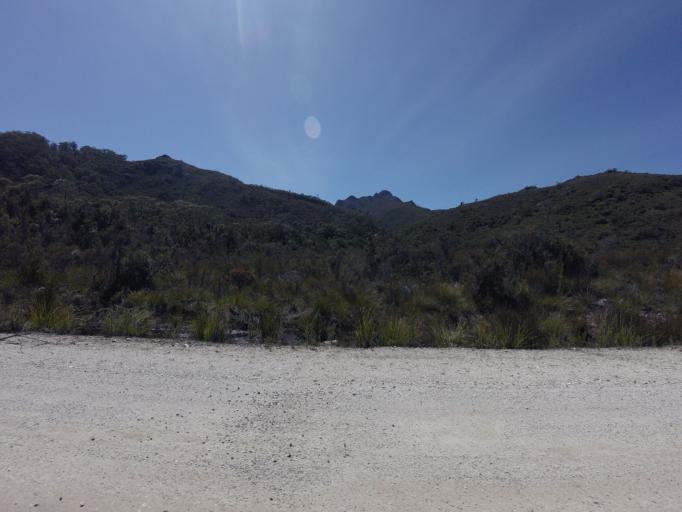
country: AU
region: Tasmania
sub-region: Huon Valley
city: Geeveston
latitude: -42.9472
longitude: 146.3522
